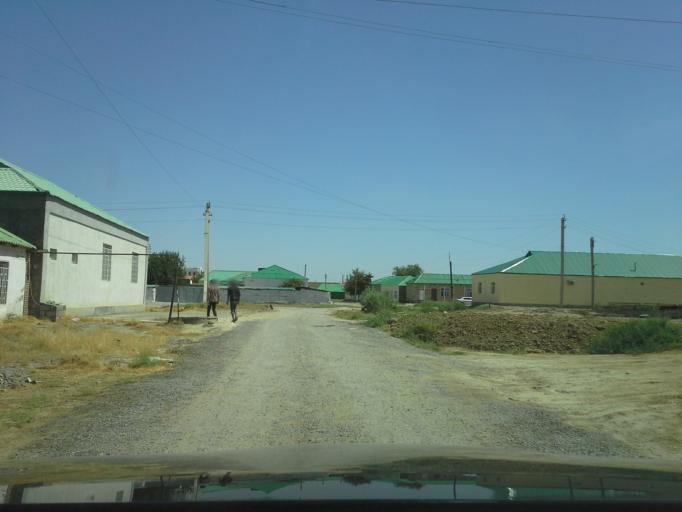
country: TM
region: Ahal
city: Ashgabat
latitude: 37.9973
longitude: 58.3186
